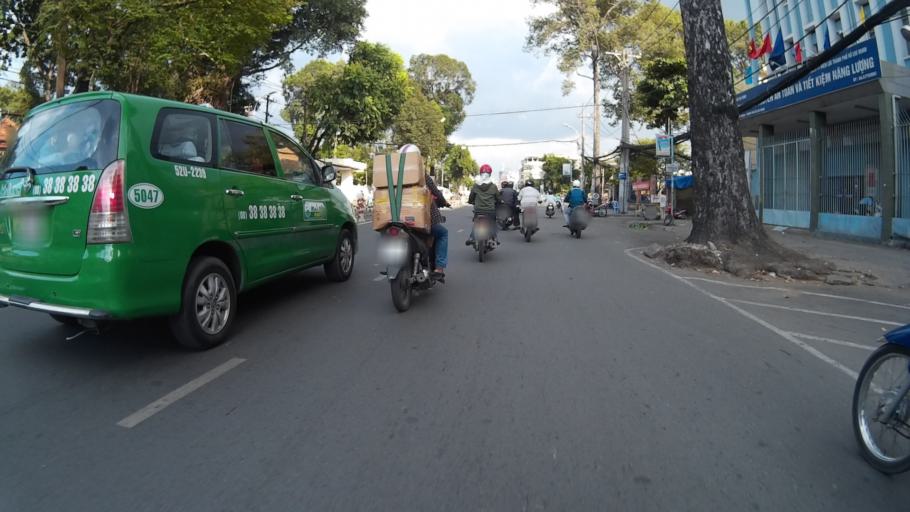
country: VN
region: Ho Chi Minh City
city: Quan Binh Thanh
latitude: 10.8026
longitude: 106.6957
